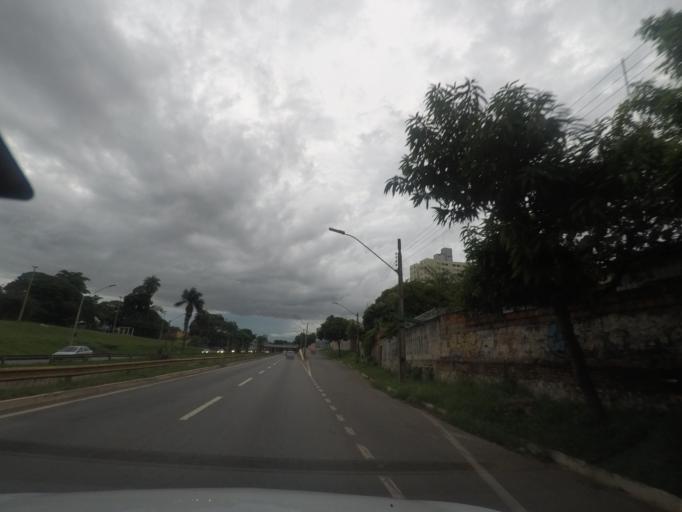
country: BR
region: Goias
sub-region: Goiania
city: Goiania
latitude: -16.6755
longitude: -49.2499
